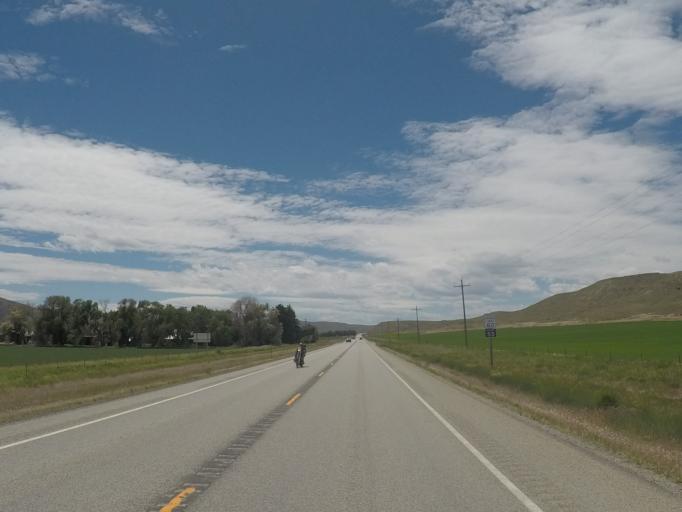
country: US
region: Montana
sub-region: Carbon County
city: Red Lodge
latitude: 45.1367
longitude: -109.0110
